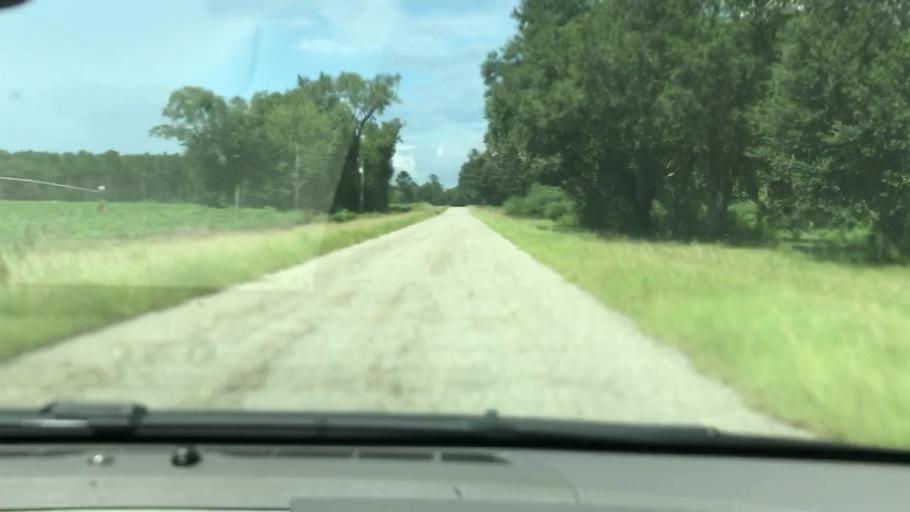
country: US
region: Georgia
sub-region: Early County
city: Blakely
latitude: 31.2164
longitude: -85.0032
